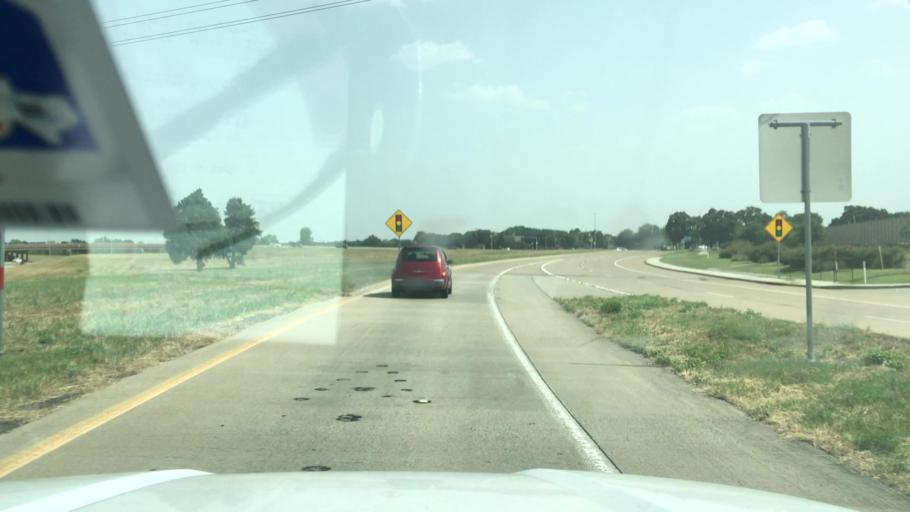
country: US
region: Texas
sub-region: Tarrant County
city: Euless
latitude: 32.8706
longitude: -97.0682
